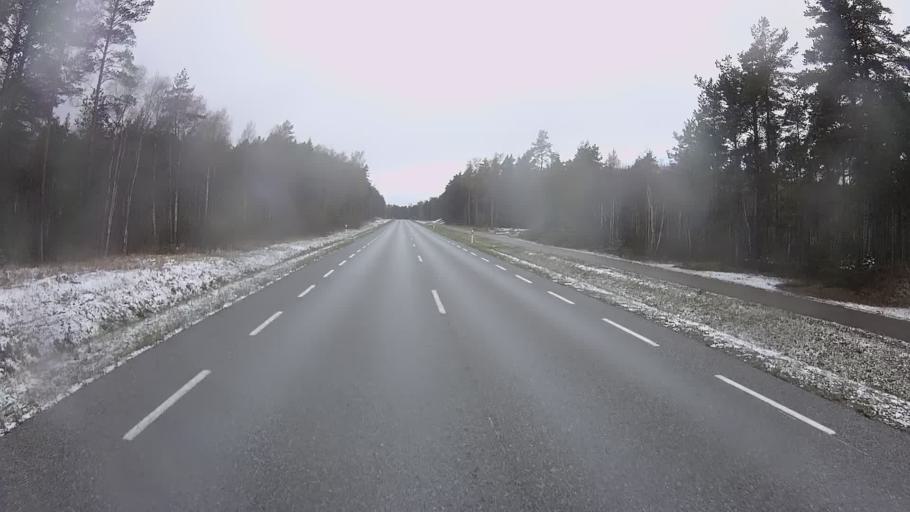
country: EE
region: Hiiumaa
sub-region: Kaerdla linn
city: Kardla
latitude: 59.0102
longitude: 22.6439
